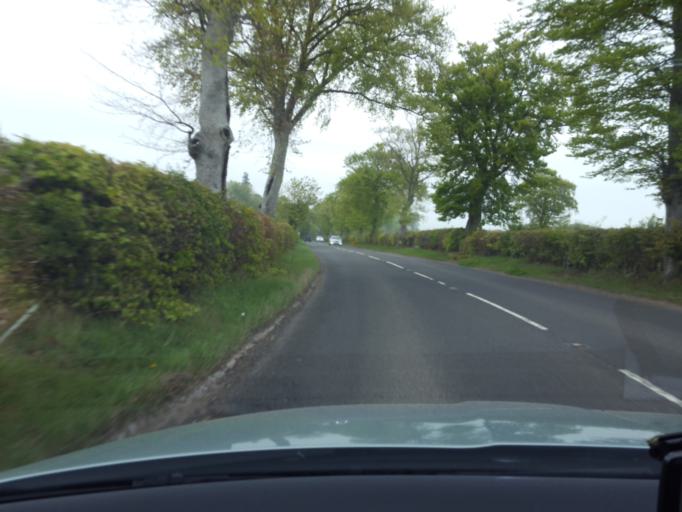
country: GB
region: Scotland
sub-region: Angus
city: Brechin
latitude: 56.7648
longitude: -2.6441
